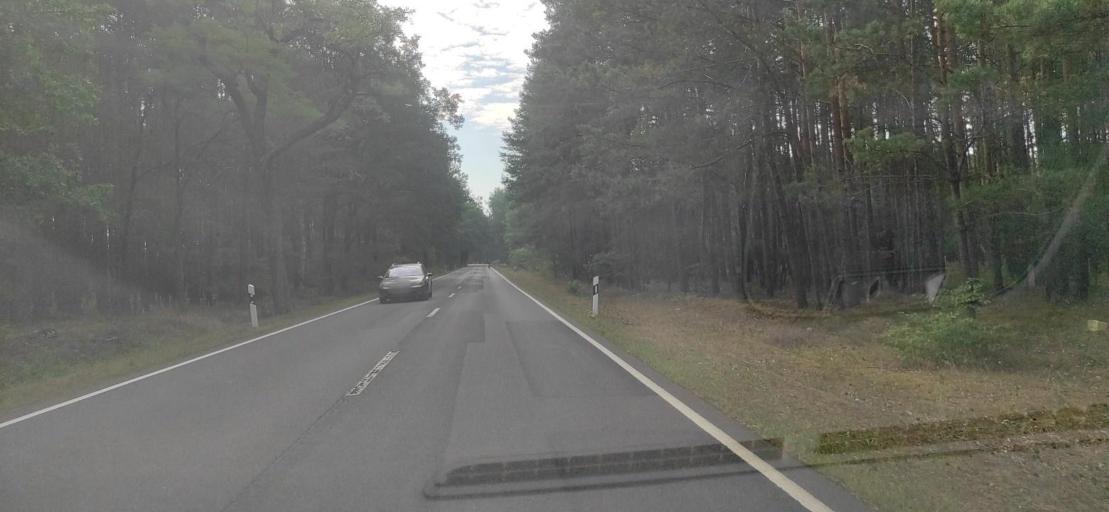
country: DE
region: Brandenburg
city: Forst
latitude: 51.7098
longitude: 14.6744
